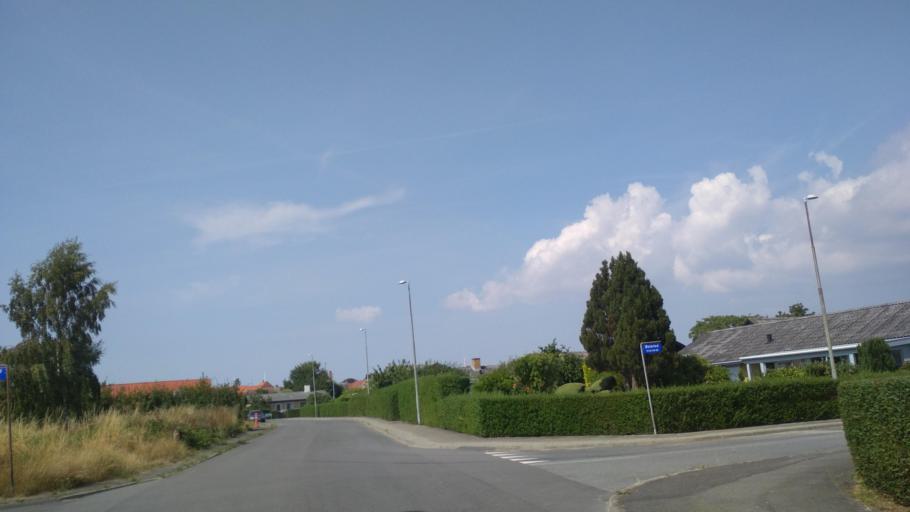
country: DK
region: Capital Region
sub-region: Bornholm Kommune
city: Akirkeby
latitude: 55.0678
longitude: 14.9283
